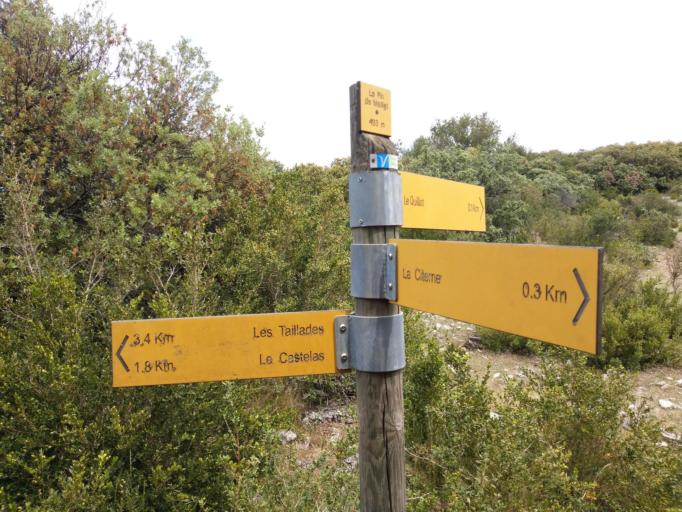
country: FR
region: Provence-Alpes-Cote d'Azur
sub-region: Departement du Vaucluse
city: Maubec
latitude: 43.8276
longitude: 5.1251
